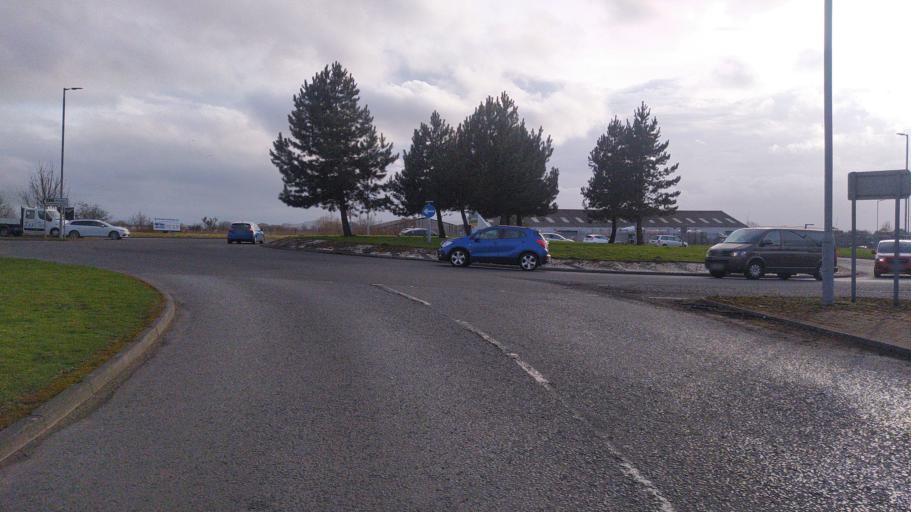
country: GB
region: Scotland
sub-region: South Ayrshire
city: Prestwick
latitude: 55.4785
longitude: -4.5969
